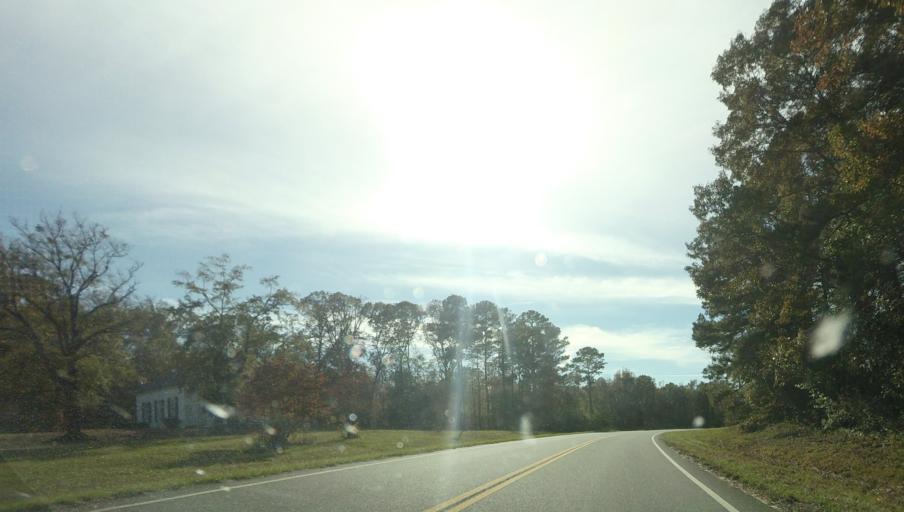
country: US
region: Georgia
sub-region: Upson County
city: Thomaston
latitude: 32.7128
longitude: -84.3561
